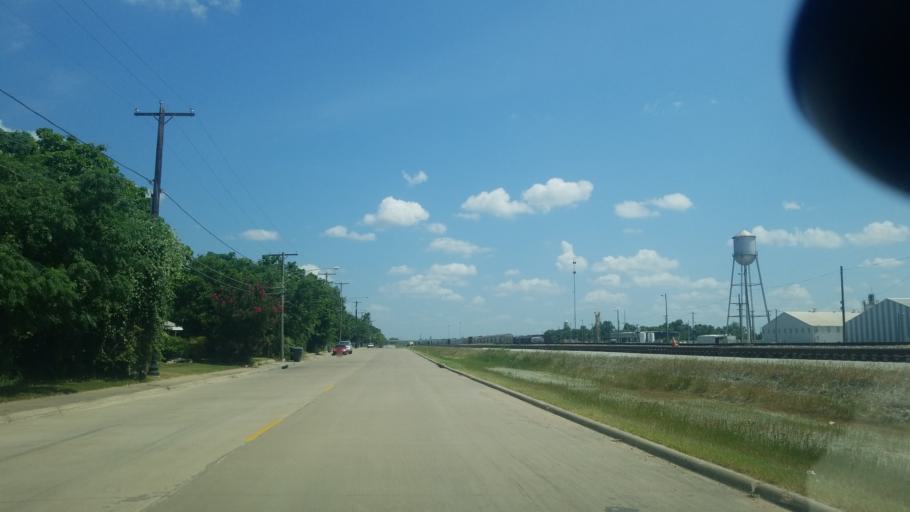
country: US
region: Texas
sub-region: Dallas County
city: Hutchins
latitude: 32.7168
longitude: -96.7511
